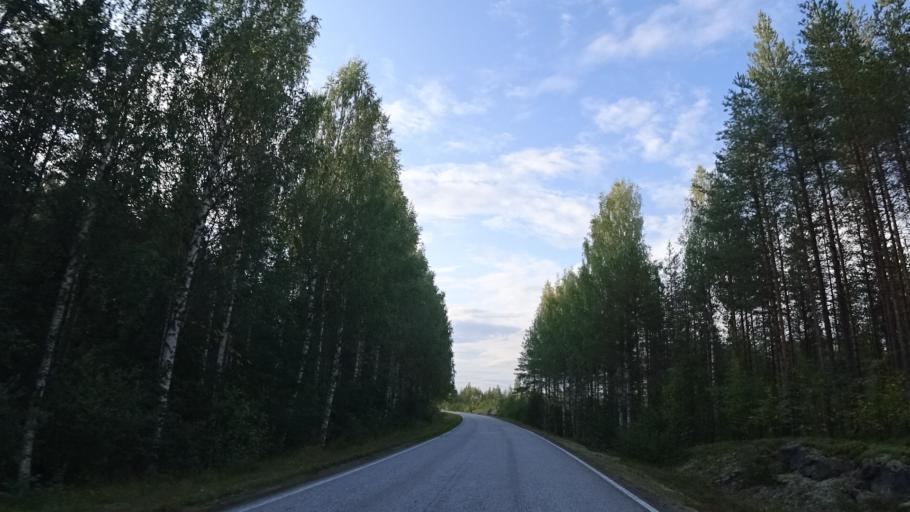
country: FI
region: North Karelia
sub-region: Pielisen Karjala
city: Lieksa
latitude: 63.3498
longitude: 30.2659
